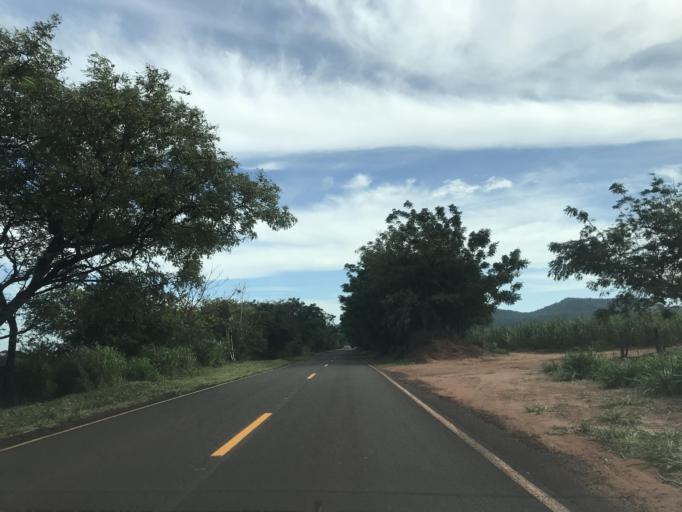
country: BR
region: Parana
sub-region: Paranavai
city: Nova Aurora
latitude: -22.8144
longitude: -52.6546
